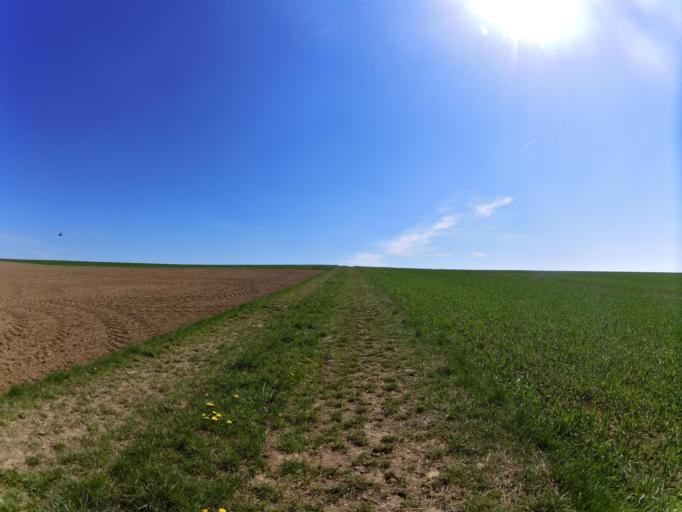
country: DE
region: Bavaria
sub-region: Regierungsbezirk Unterfranken
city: Winterhausen
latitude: 49.6862
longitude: 9.9933
